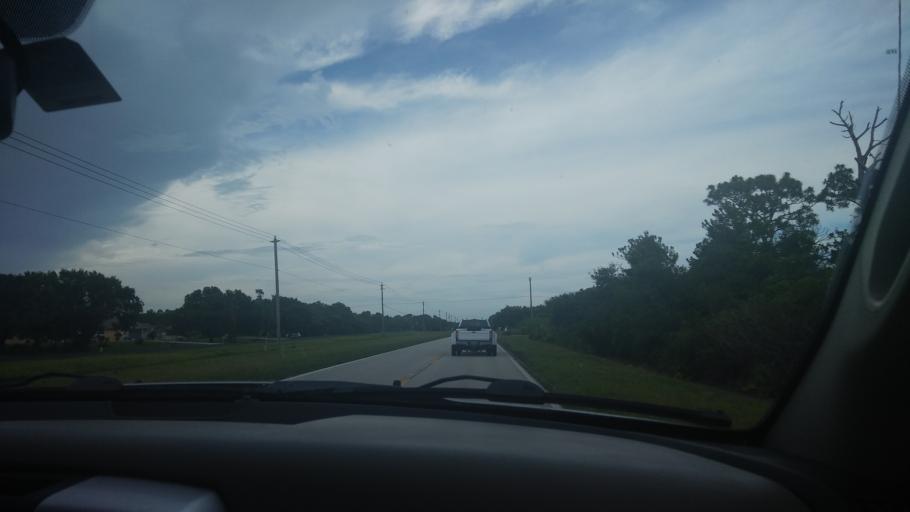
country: US
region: Florida
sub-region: Brevard County
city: Grant-Valkaria
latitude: 27.9271
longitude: -80.6229
